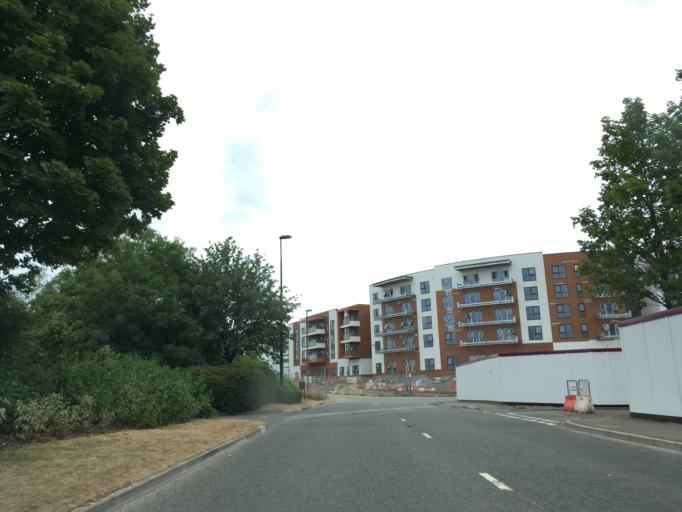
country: GB
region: England
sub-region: South Gloucestershire
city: Stoke Gifford
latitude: 51.5009
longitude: -2.5413
